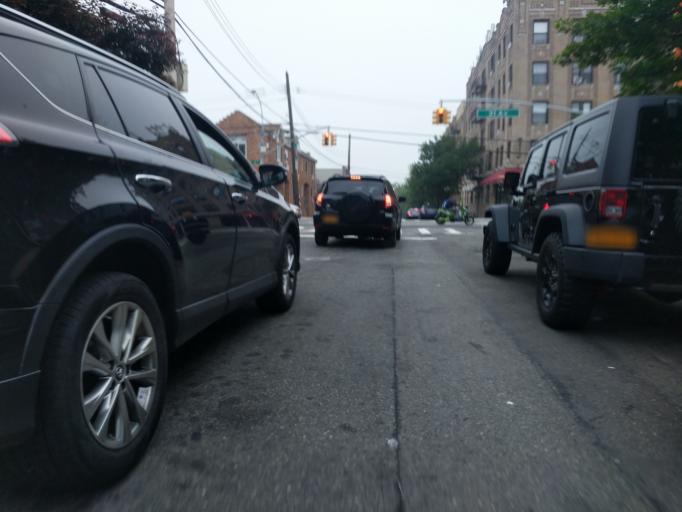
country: US
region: New York
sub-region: Queens County
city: Long Island City
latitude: 40.7609
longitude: -73.9153
